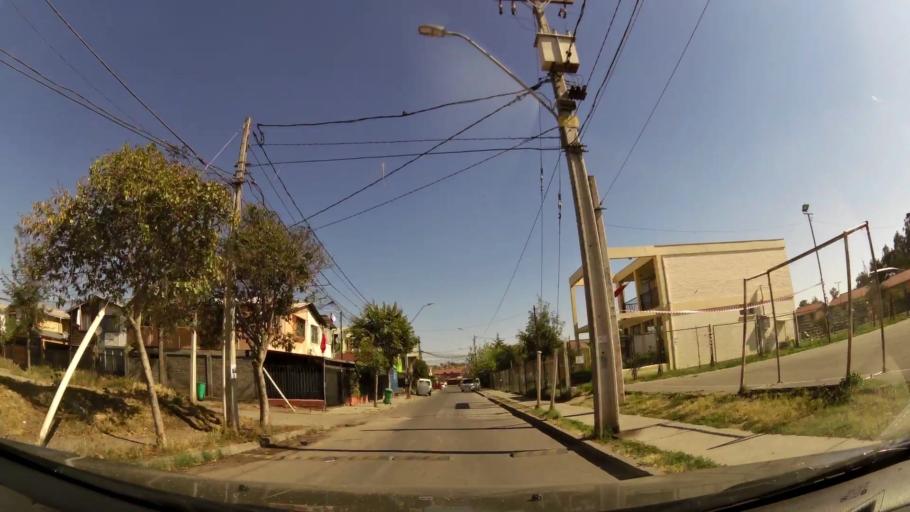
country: CL
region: Santiago Metropolitan
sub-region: Provincia de Maipo
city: San Bernardo
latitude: -33.6145
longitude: -70.7054
